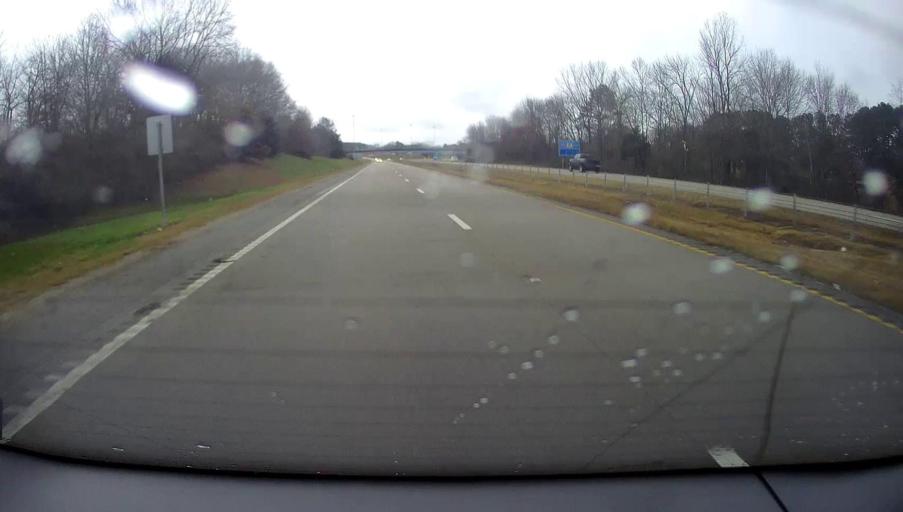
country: US
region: Mississippi
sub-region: Alcorn County
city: Corinth
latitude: 34.9246
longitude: -88.5448
